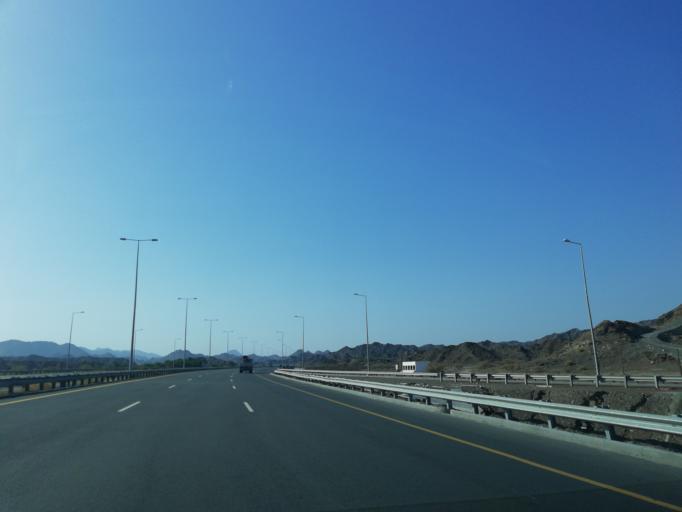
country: OM
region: Muhafazat ad Dakhiliyah
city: Sufalat Sama'il
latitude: 23.0159
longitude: 58.2203
